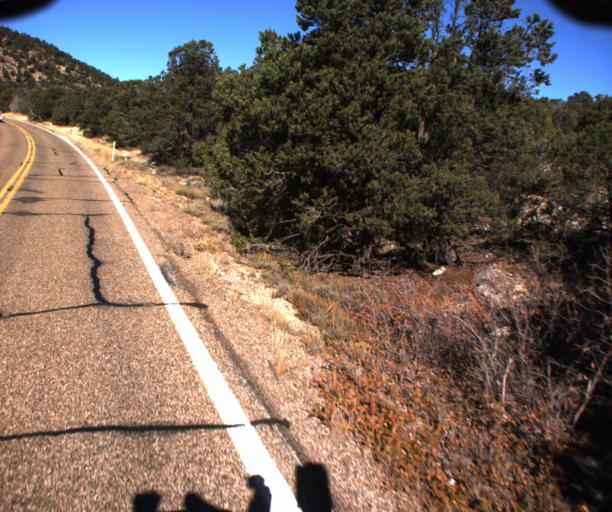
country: US
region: Arizona
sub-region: Coconino County
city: Fredonia
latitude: 36.7427
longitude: -112.1107
